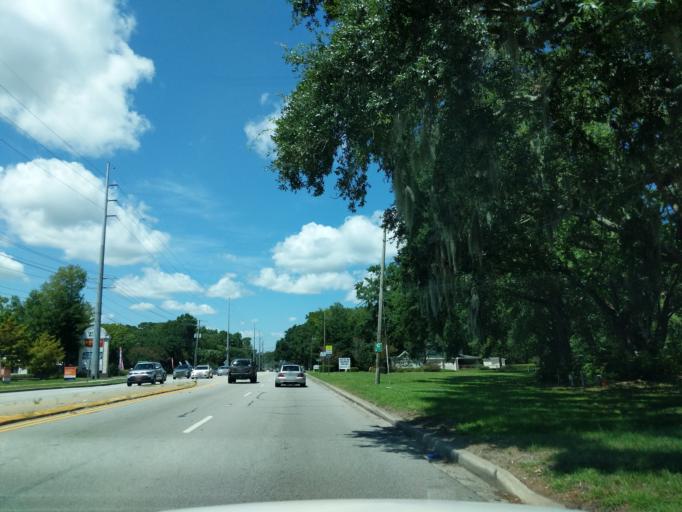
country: US
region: South Carolina
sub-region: Charleston County
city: Folly Beach
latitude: 32.7173
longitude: -79.9657
